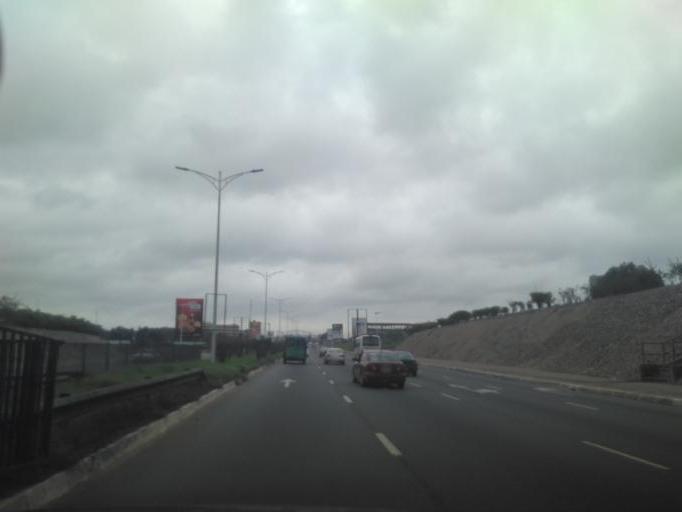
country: GH
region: Greater Accra
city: Medina Estates
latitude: 5.6232
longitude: -0.1764
